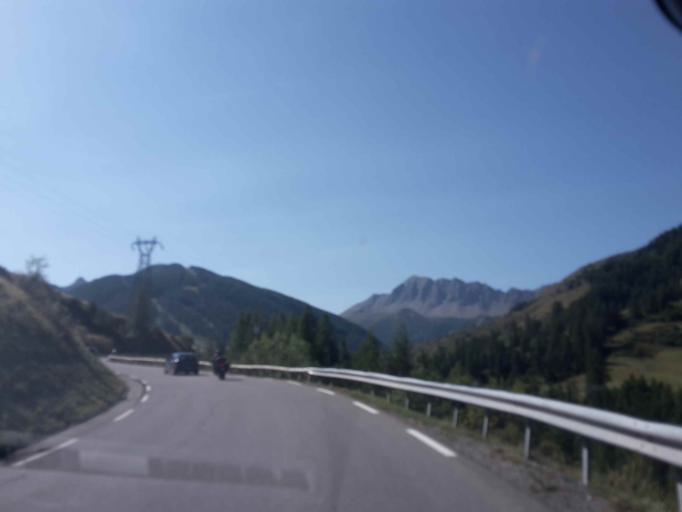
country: FR
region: Provence-Alpes-Cote d'Azur
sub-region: Departement des Hautes-Alpes
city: Guillestre
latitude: 44.6036
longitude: 6.6886
